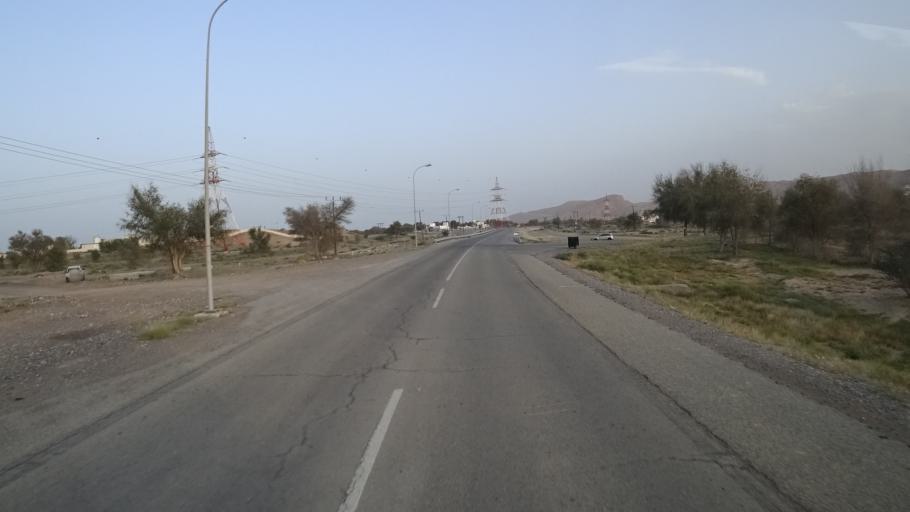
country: OM
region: Muhafazat Masqat
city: Muscat
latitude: 23.2077
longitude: 58.9482
